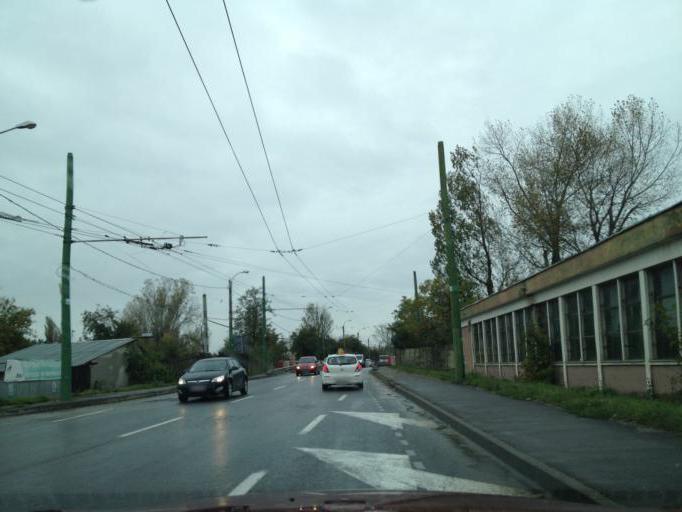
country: RO
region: Brasov
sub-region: Comuna Sanpetru
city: Sanpetru
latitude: 45.6828
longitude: 25.6157
